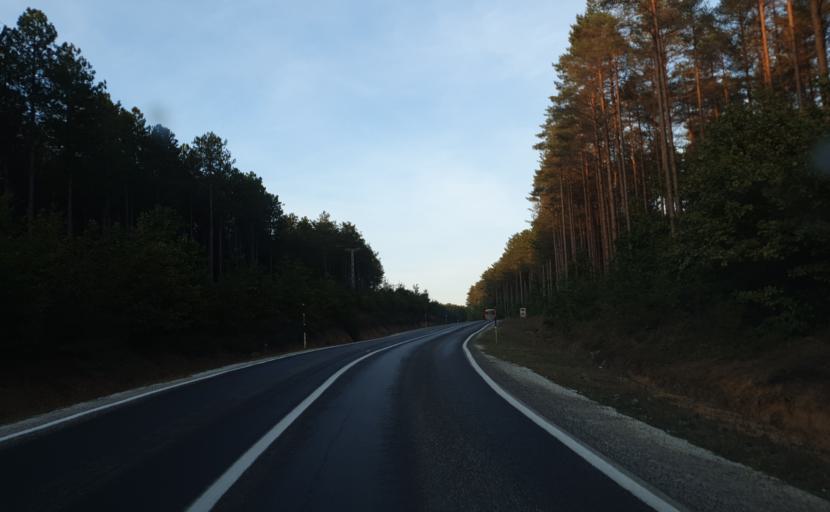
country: TR
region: Kirklareli
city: Igneada
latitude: 41.8550
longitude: 27.8075
